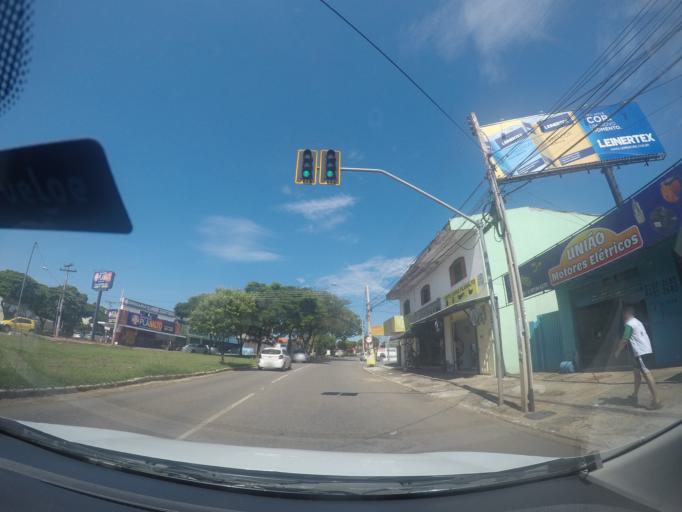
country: BR
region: Goias
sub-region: Goiania
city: Goiania
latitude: -16.7112
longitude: -49.3002
